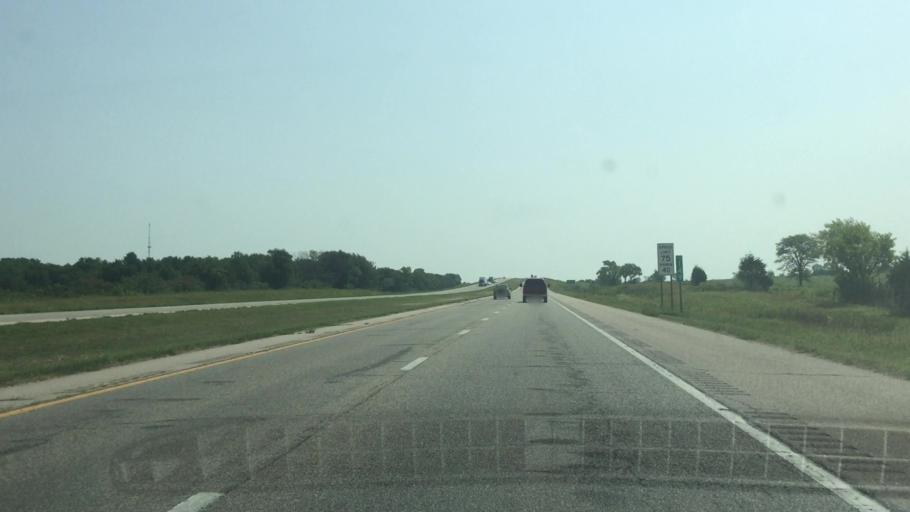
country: US
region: Kansas
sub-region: Osage County
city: Osage City
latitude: 38.4263
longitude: -95.8474
